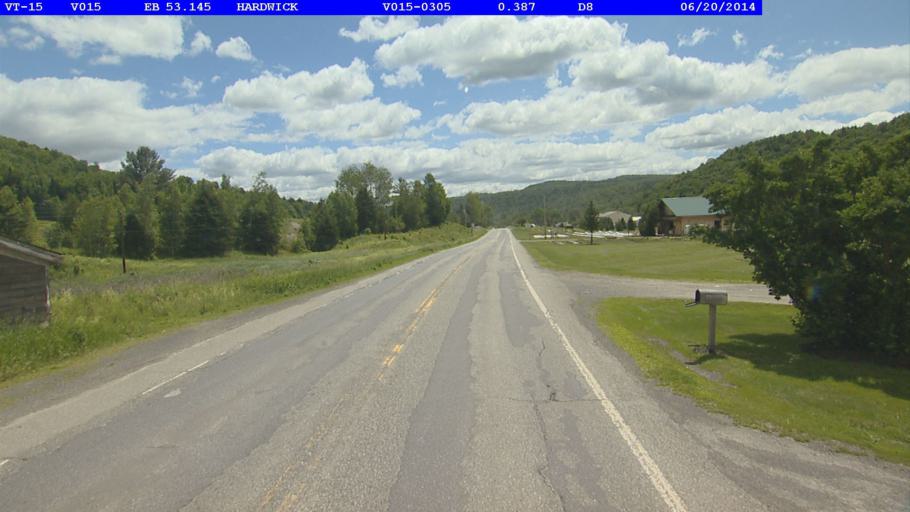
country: US
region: Vermont
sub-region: Caledonia County
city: Hardwick
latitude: 44.5217
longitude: -72.4130
